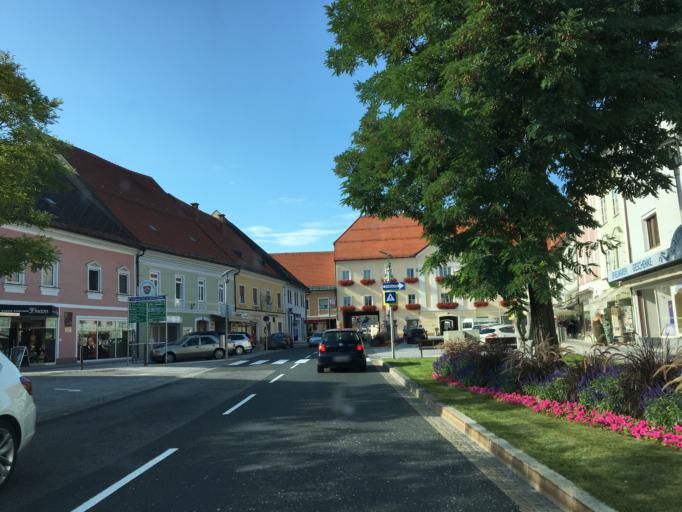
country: AT
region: Carinthia
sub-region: Politischer Bezirk Volkermarkt
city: Voelkermarkt
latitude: 46.6597
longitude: 14.6341
